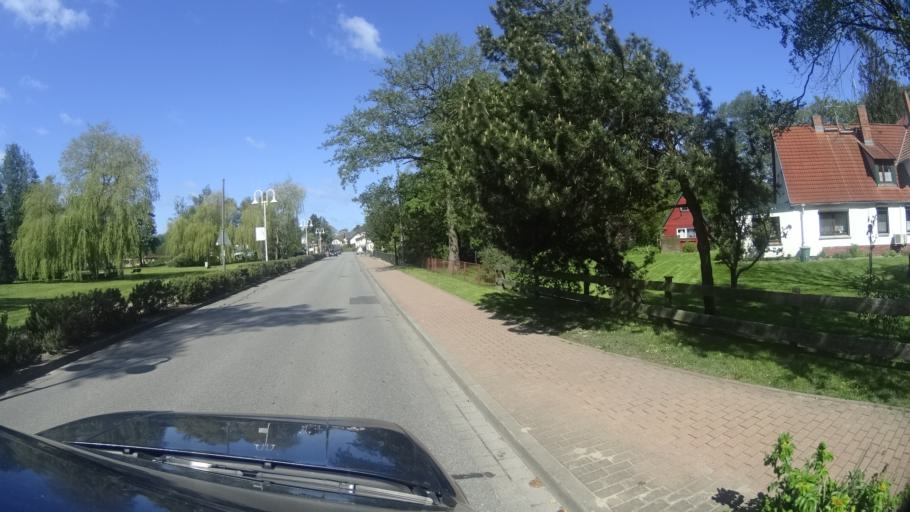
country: DE
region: Mecklenburg-Vorpommern
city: Ostseebad Prerow
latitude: 54.4465
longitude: 12.5739
